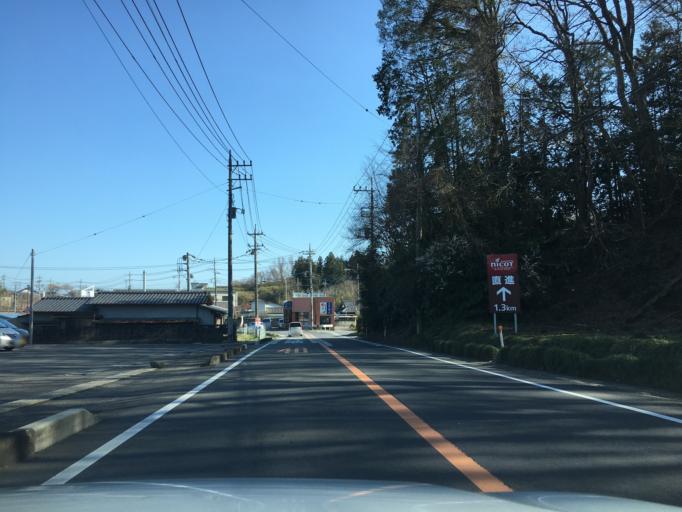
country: JP
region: Ibaraki
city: Omiya
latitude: 36.5452
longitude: 140.3322
